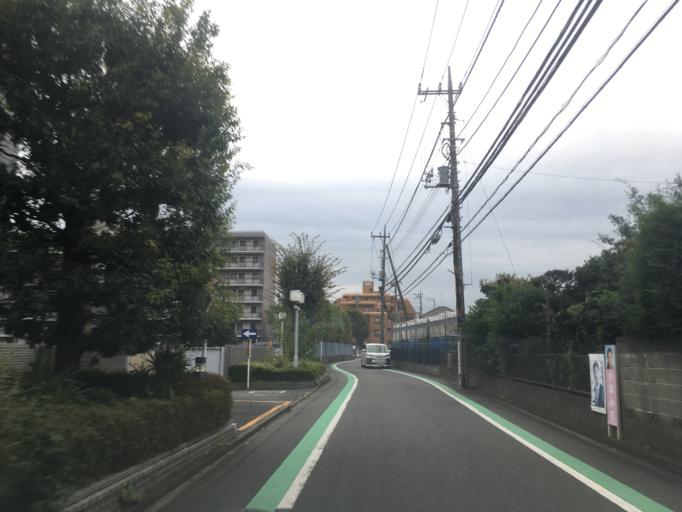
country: JP
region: Tokyo
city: Higashimurayama-shi
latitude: 35.7570
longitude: 139.4628
